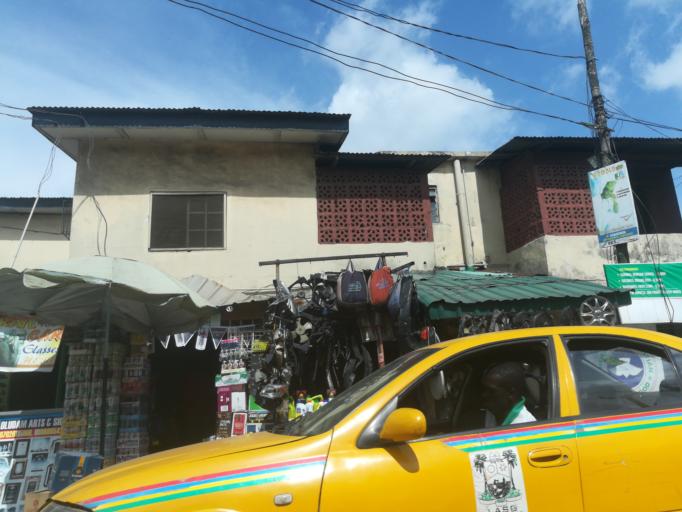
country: NG
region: Lagos
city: Somolu
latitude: 6.5303
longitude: 3.3804
